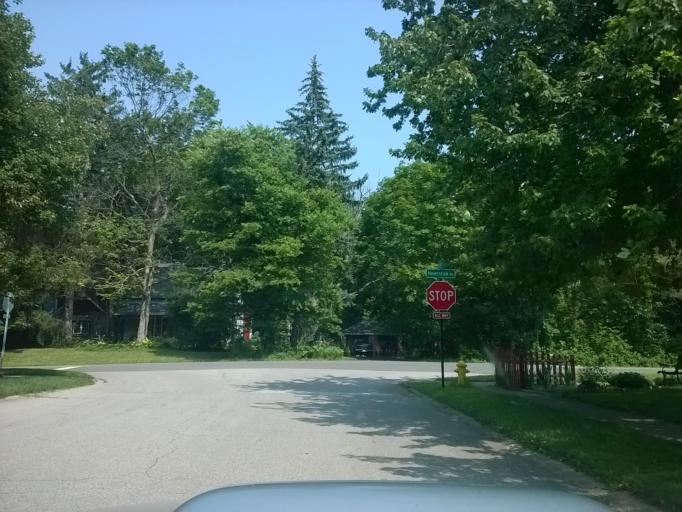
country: US
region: Indiana
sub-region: Hamilton County
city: Carmel
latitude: 39.9483
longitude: -86.0986
